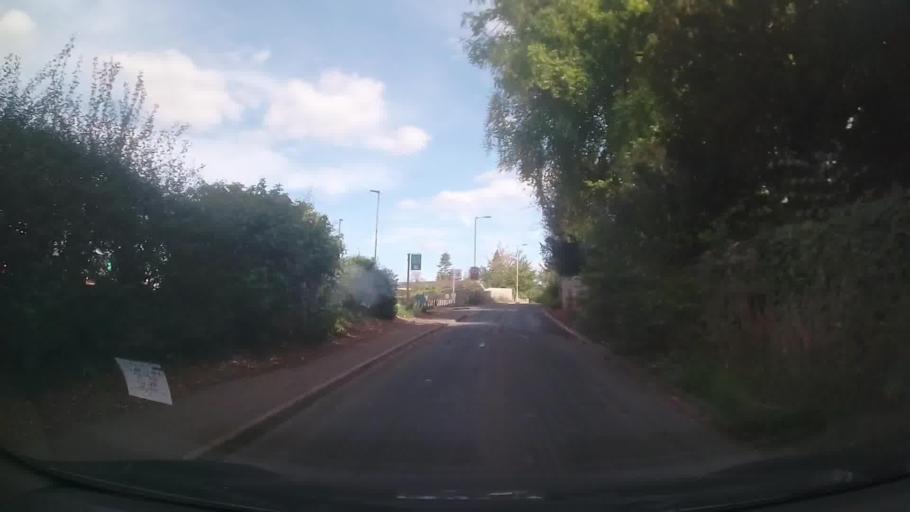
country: GB
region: England
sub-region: Shropshire
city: Pontesbury
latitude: 52.6503
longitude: -2.8884
